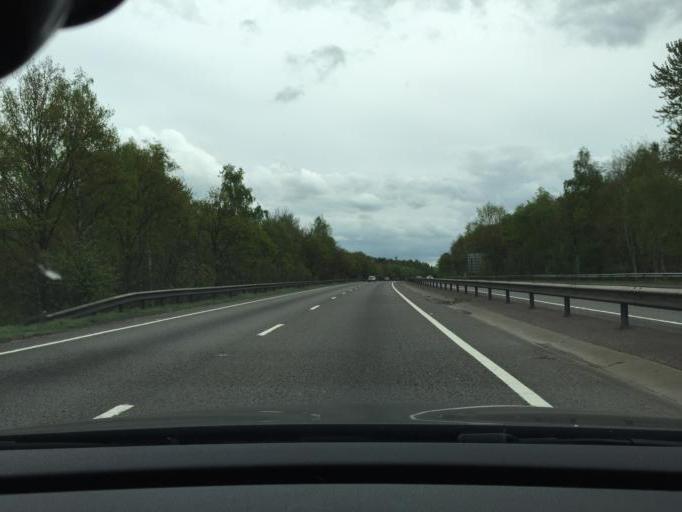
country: GB
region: England
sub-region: Oxfordshire
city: Radley
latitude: 51.7164
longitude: -1.2539
